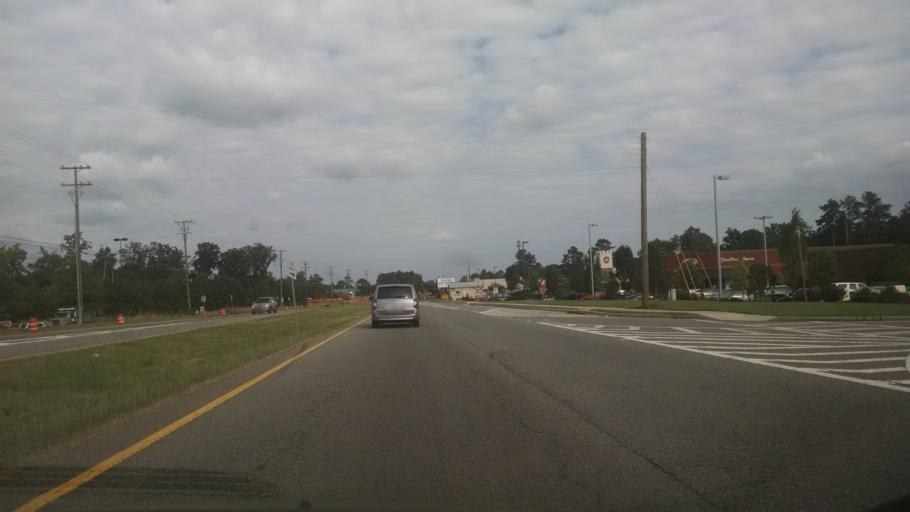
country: US
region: Georgia
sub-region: Forsyth County
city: Cumming
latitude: 34.1621
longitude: -84.1160
